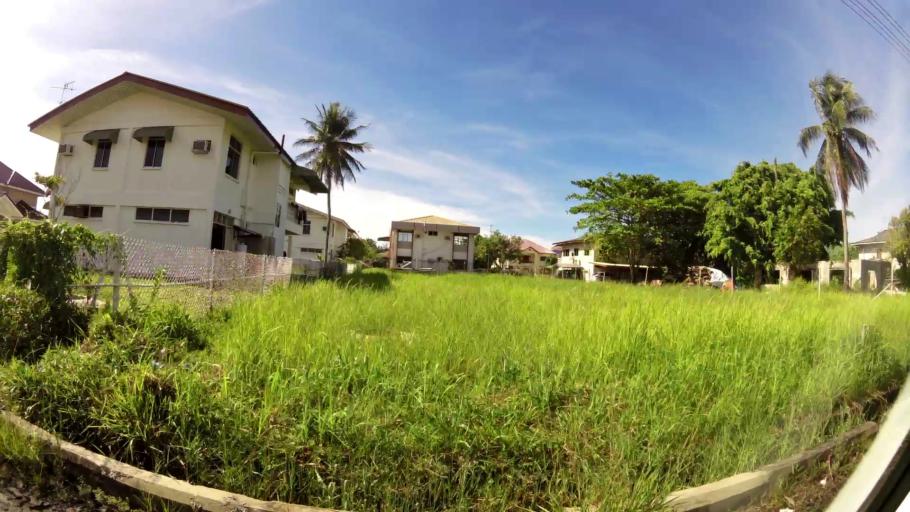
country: BN
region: Belait
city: Kuala Belait
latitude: 4.5864
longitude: 114.2091
